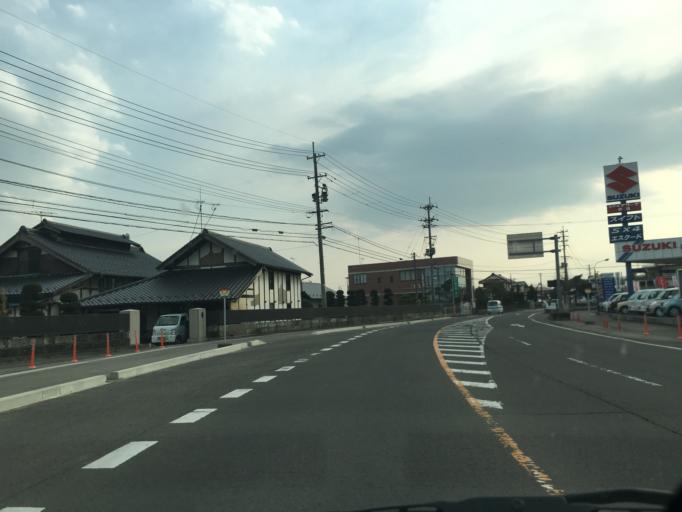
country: JP
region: Fukushima
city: Yanagawamachi-saiwaicho
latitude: 37.8482
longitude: 140.5920
